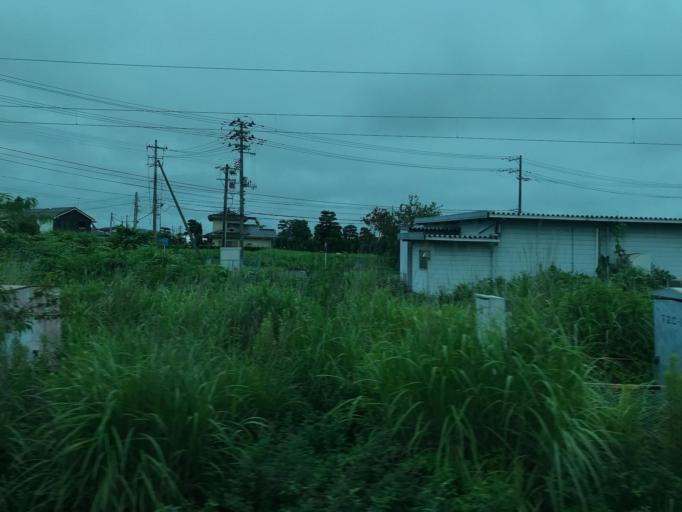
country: JP
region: Tochigi
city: Kuroiso
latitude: 37.0986
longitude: 140.1862
